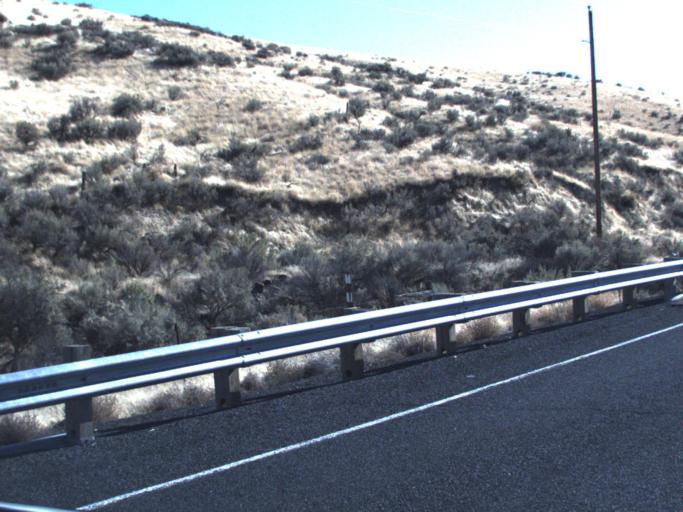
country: US
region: Washington
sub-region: Franklin County
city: Connell
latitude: 46.6684
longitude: -118.5471
